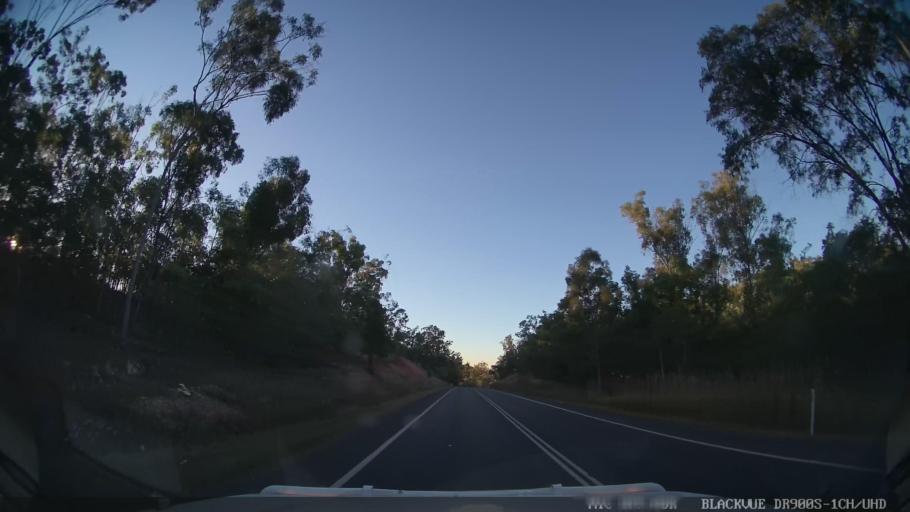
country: AU
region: Queensland
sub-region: Gladstone
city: Toolooa
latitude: -23.9656
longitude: 151.2175
